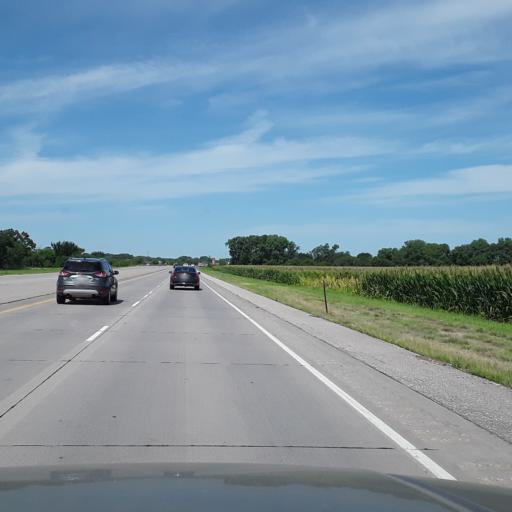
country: US
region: Nebraska
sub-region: Lancaster County
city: Lincoln
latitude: 40.8797
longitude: -96.7698
